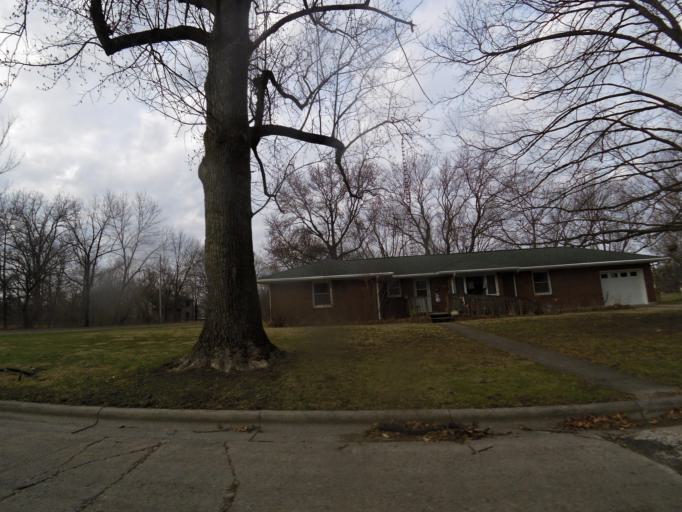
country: US
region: Illinois
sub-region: Christian County
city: Pana
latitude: 39.3762
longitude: -89.0830
